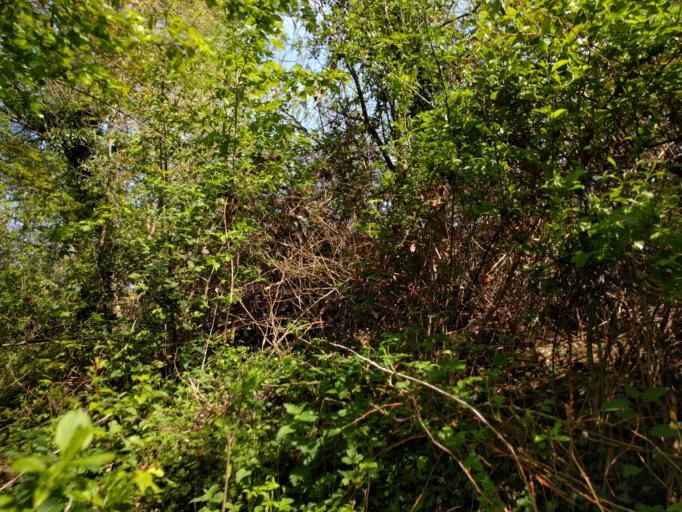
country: DK
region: South Denmark
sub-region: Kerteminde Kommune
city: Langeskov
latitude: 55.3890
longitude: 10.5615
